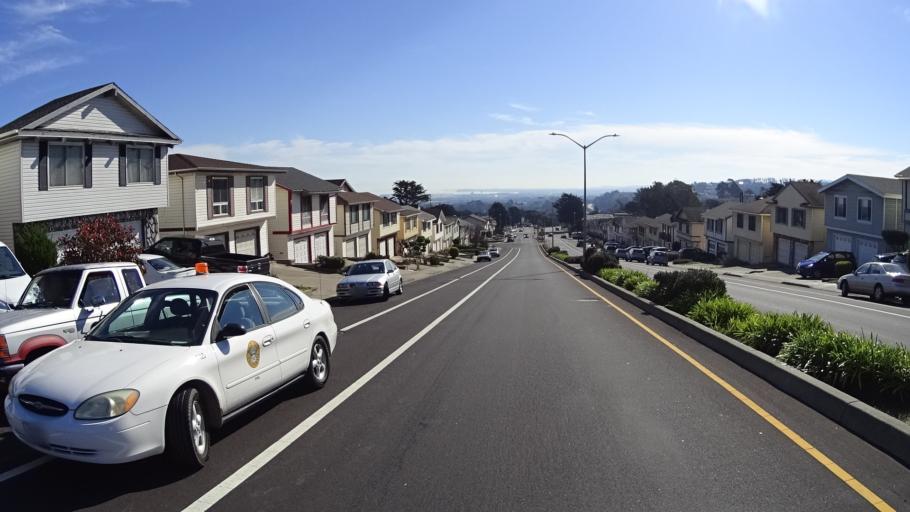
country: US
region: California
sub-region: San Mateo County
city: Colma
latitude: 37.6519
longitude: -122.4578
